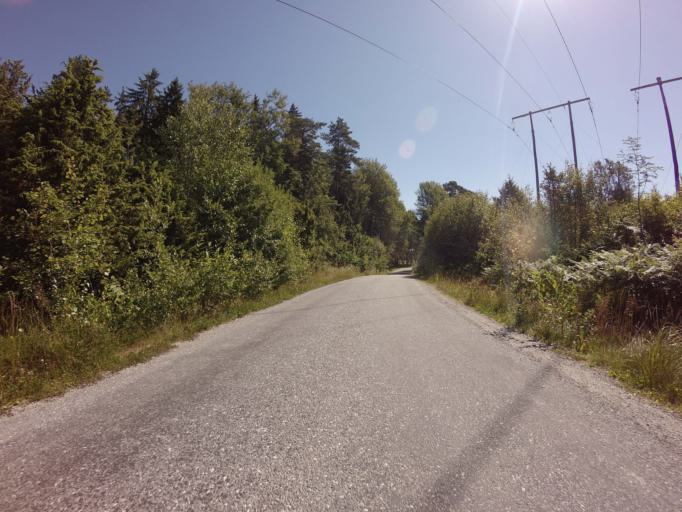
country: SE
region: Stockholm
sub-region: Jarfalla Kommun
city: Jakobsberg
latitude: 59.4644
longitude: 17.8768
